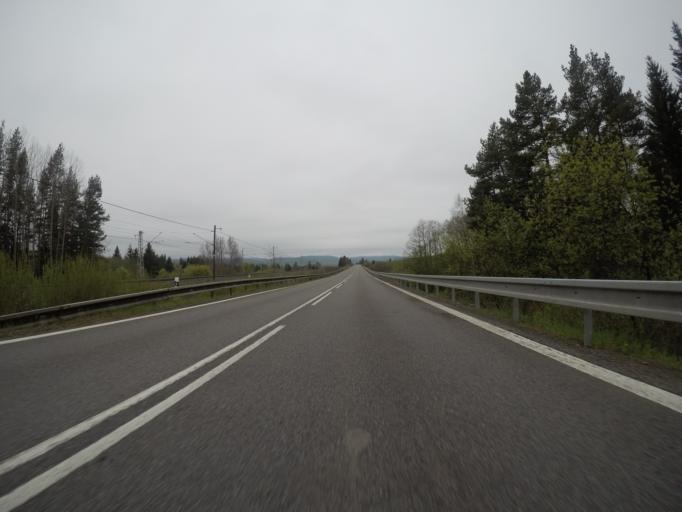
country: SK
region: Presovsky
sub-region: Okres Poprad
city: Strba
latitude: 49.0847
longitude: 20.0550
